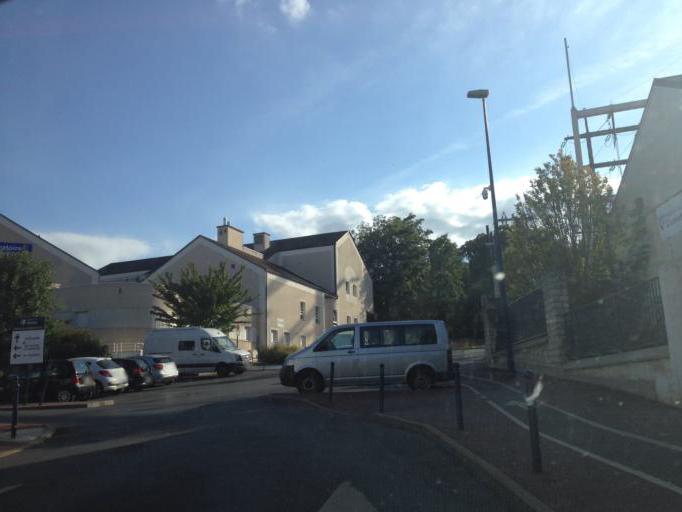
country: FR
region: Ile-de-France
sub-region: Departement des Hauts-de-Seine
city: Clamart
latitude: 48.7996
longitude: 2.2601
